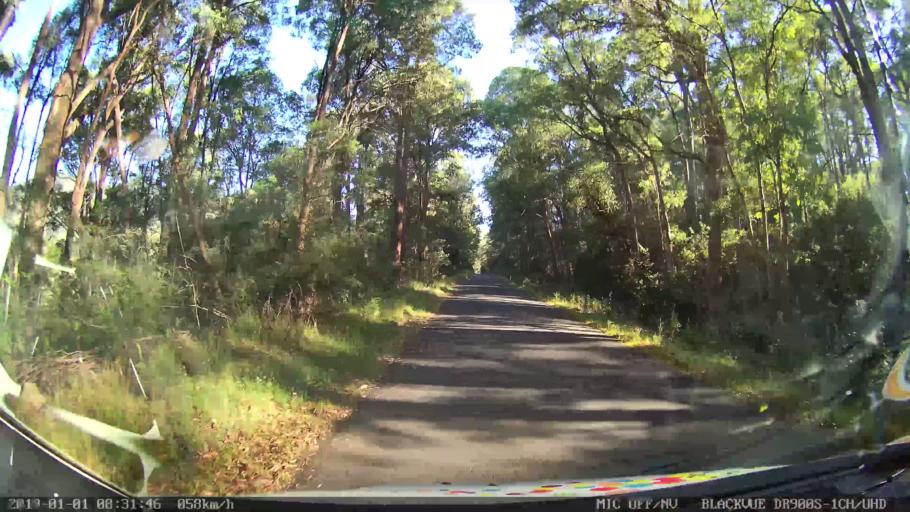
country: AU
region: New South Wales
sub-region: Snowy River
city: Jindabyne
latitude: -36.3676
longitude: 148.2054
